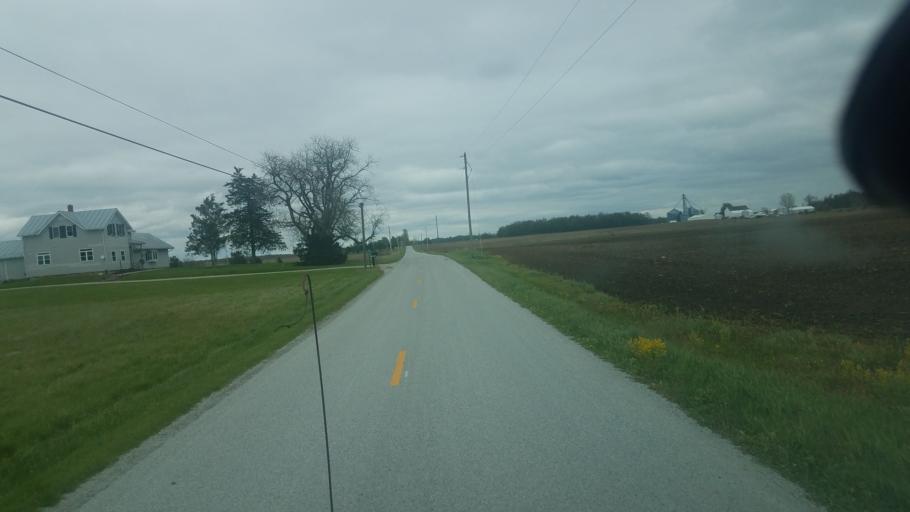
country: US
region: Ohio
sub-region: Hardin County
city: Kenton
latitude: 40.6575
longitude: -83.4860
